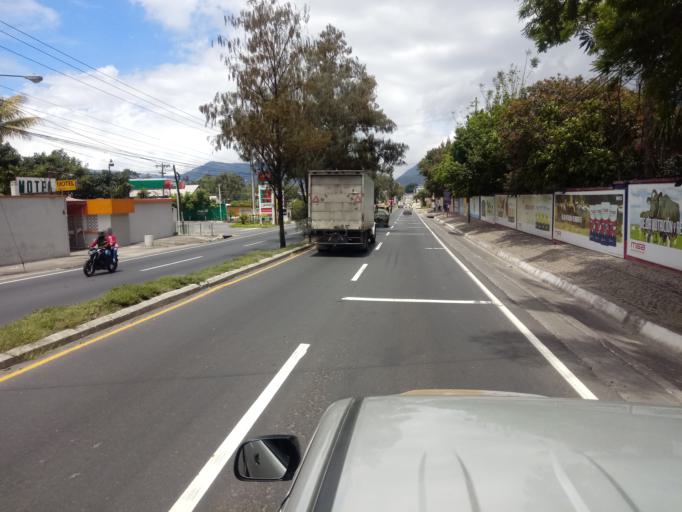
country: GT
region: Guatemala
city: Amatitlan
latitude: 14.4874
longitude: -90.6261
